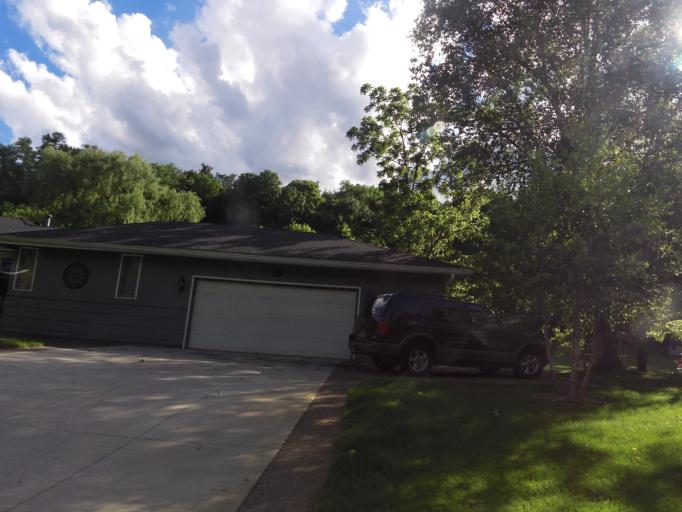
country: US
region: Minnesota
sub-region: Carver County
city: Chaska
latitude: 44.7918
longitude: -93.6098
